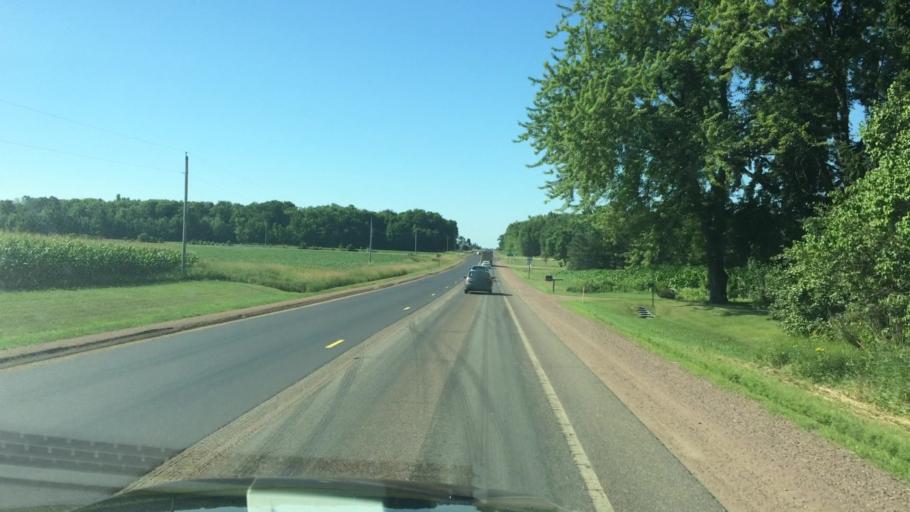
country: US
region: Wisconsin
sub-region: Marathon County
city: Stratford
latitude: 44.8618
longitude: -90.0791
